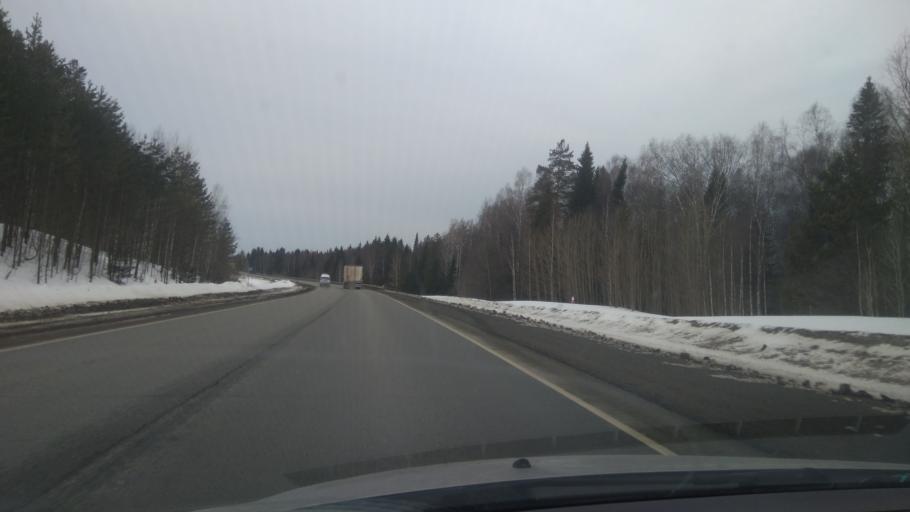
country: RU
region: Sverdlovsk
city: Ufimskiy
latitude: 56.7863
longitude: 58.3873
